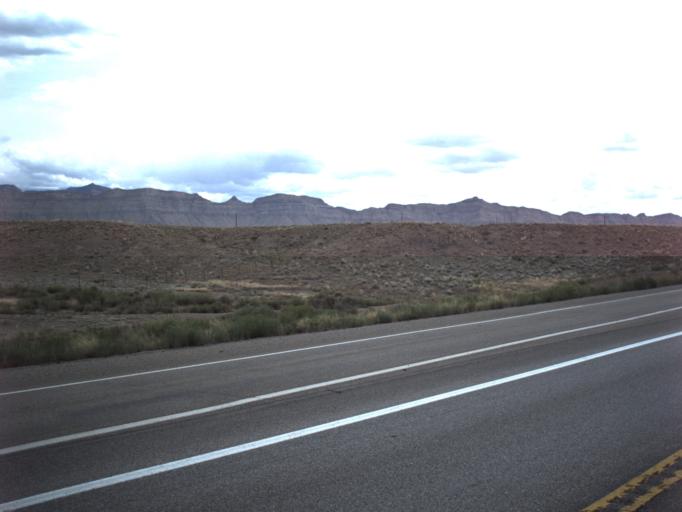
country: US
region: Utah
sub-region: Carbon County
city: East Carbon City
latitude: 39.3736
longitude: -110.3999
